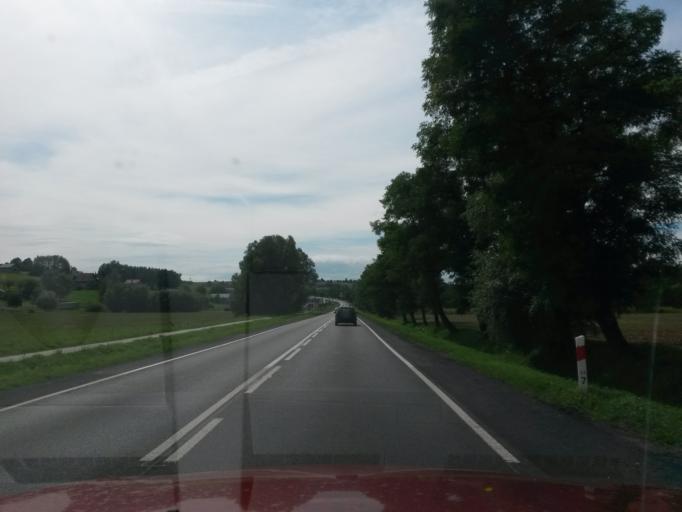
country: PL
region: Lesser Poland Voivodeship
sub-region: Powiat brzeski
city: Gnojnik
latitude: 49.8916
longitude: 20.6087
